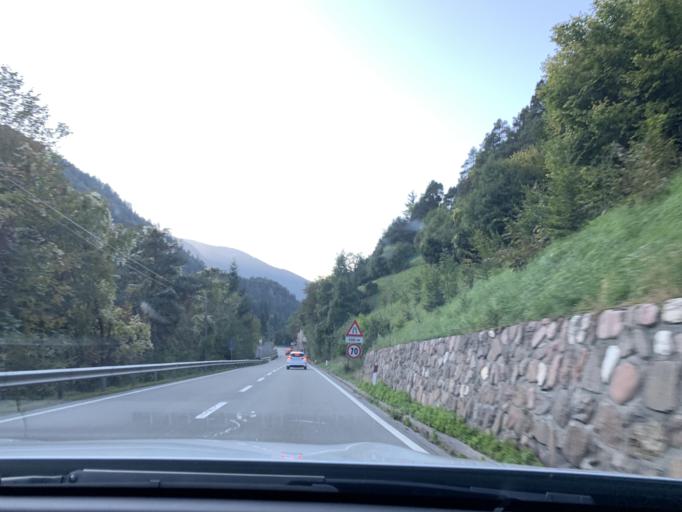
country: IT
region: Trentino-Alto Adige
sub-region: Bolzano
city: Nova Ponente
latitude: 46.4479
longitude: 11.4522
